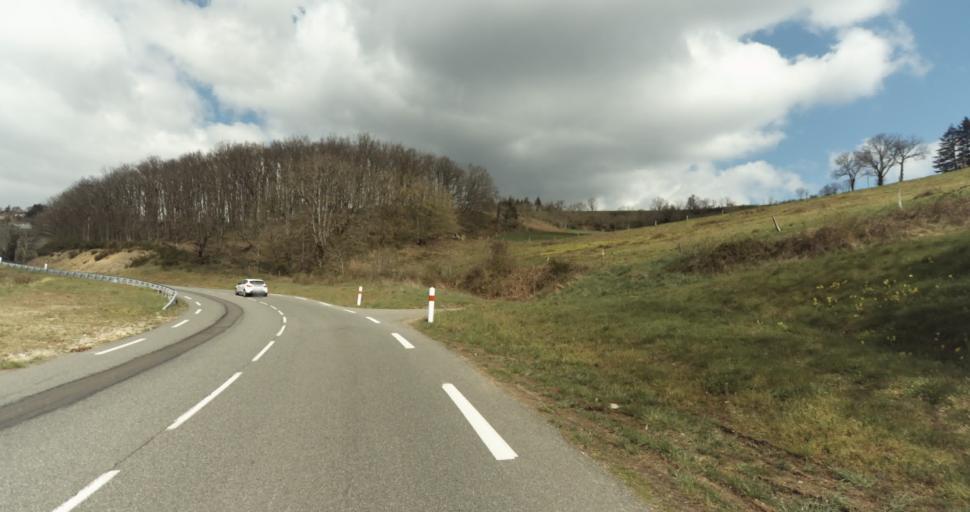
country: FR
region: Rhone-Alpes
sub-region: Departement du Rhone
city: Tarare
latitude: 45.9287
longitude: 4.3987
